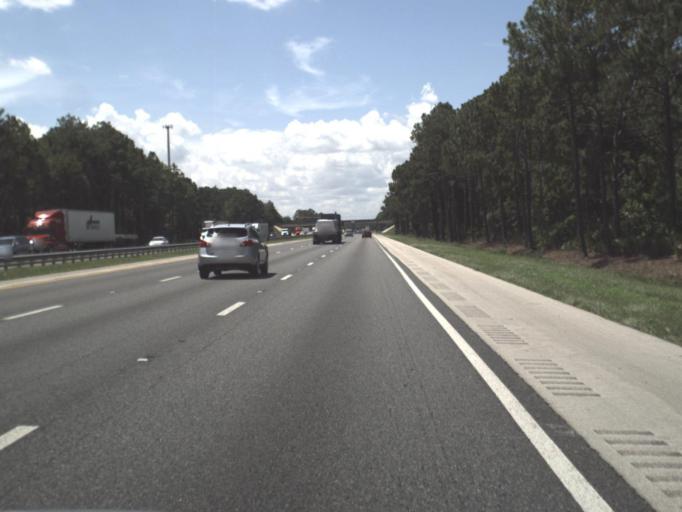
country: US
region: Florida
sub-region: Saint Johns County
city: Saint Augustine South
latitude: 29.8660
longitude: -81.3966
